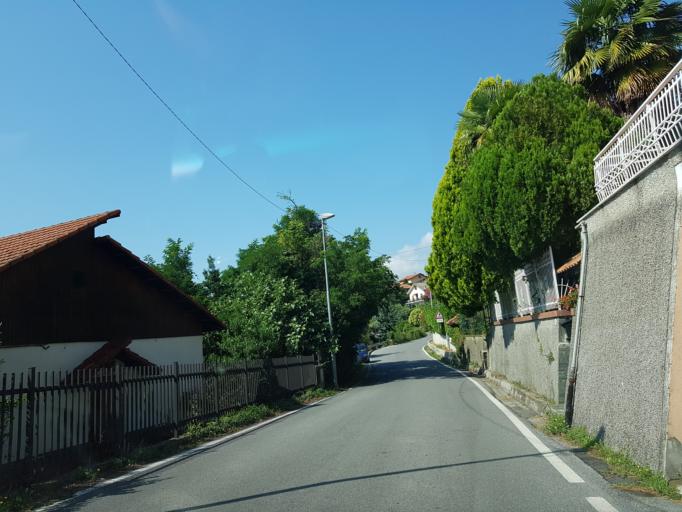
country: IT
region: Liguria
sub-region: Provincia di Genova
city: Pedemonte
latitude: 44.4935
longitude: 8.9144
